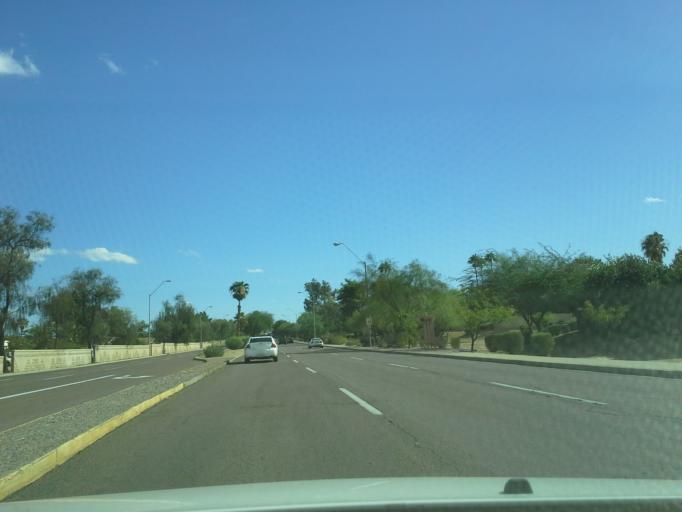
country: US
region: Arizona
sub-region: Maricopa County
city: Glendale
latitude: 33.6075
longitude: -112.0808
